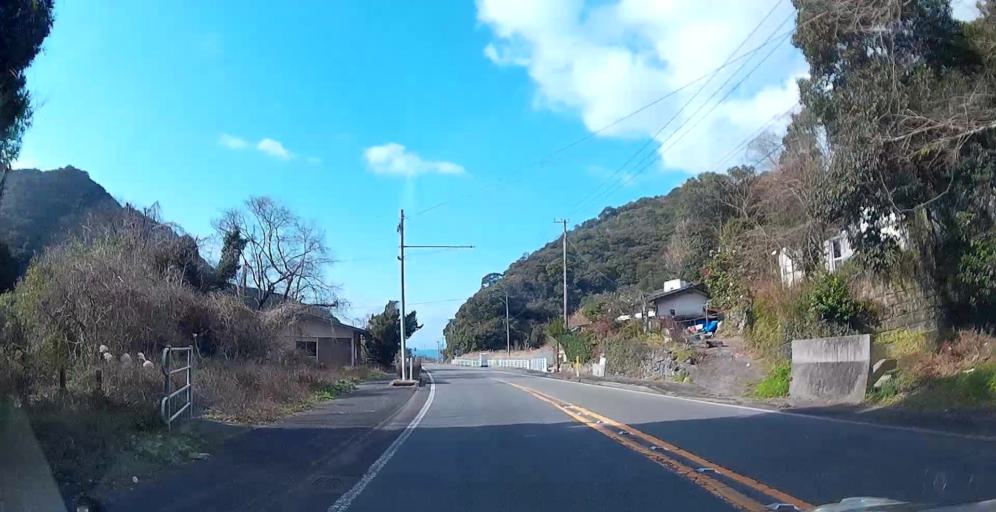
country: JP
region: Kumamoto
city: Yatsushiro
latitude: 32.4122
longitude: 130.5540
